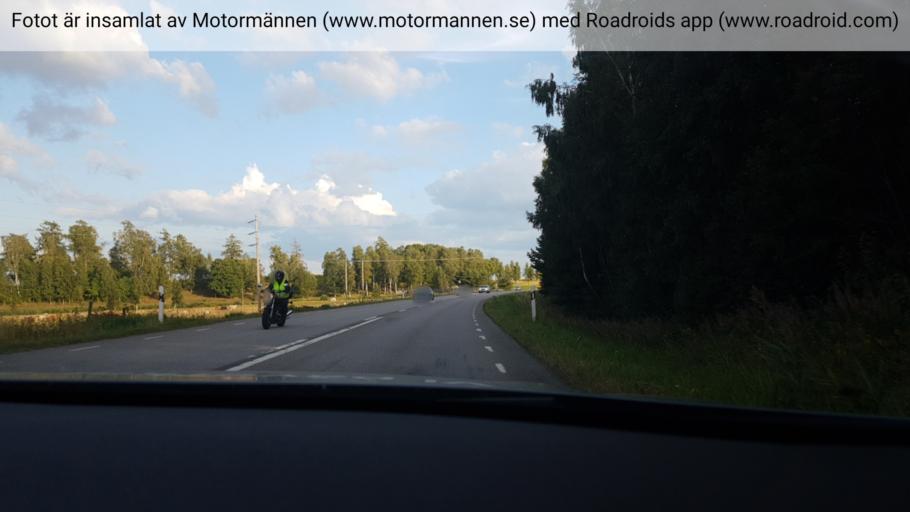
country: SE
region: Vaestra Goetaland
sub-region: Skara Kommun
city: Skara
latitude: 58.2869
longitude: 13.4816
